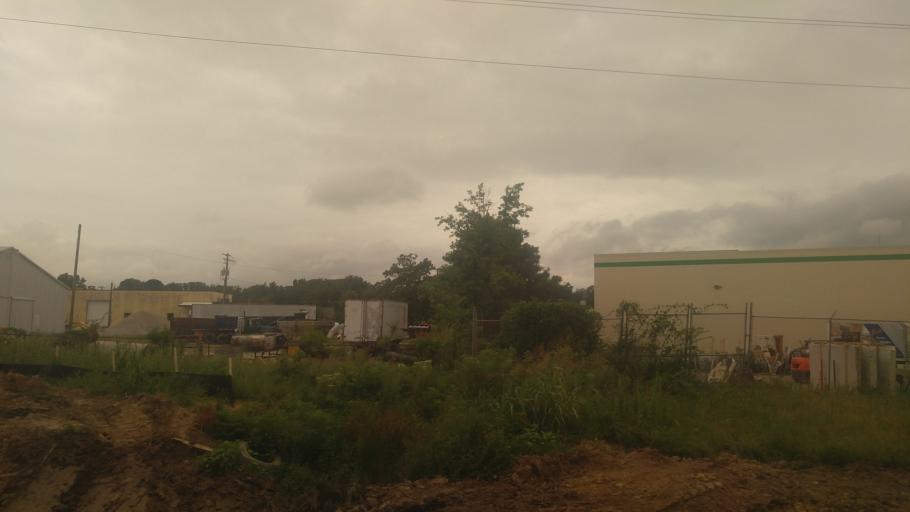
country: US
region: Virginia
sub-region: Henrico County
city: Dumbarton
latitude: 37.6107
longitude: -77.4929
